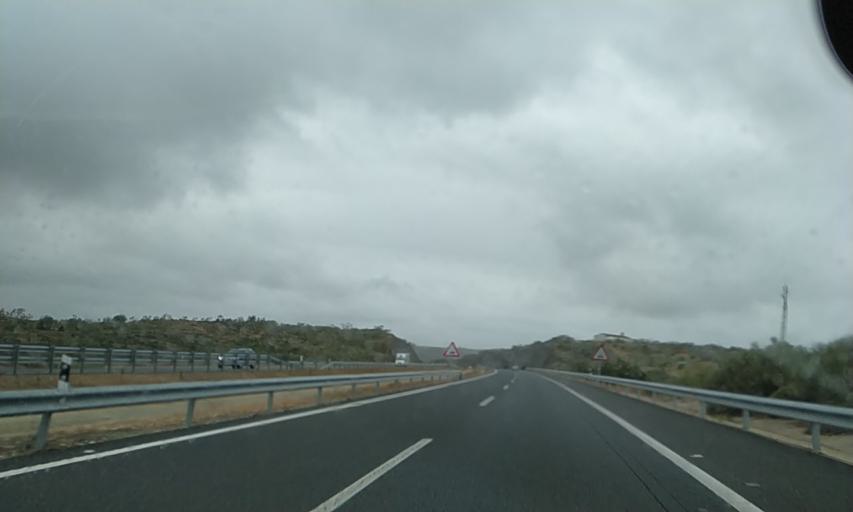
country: ES
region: Extremadura
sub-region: Provincia de Caceres
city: Canaveral
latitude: 39.7350
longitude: -6.4111
